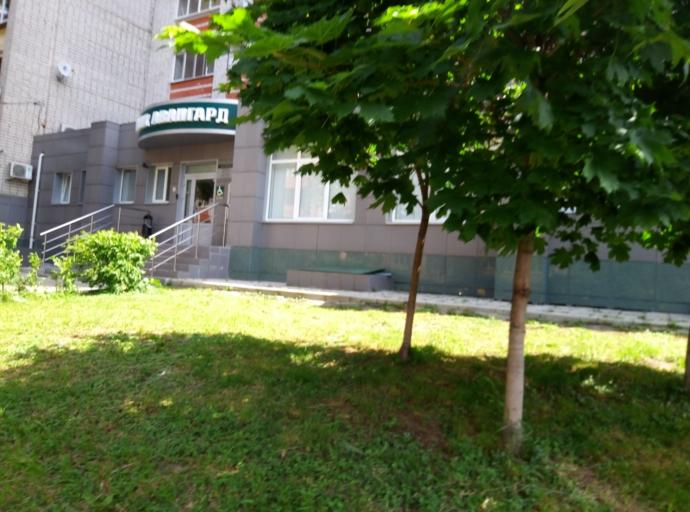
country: RU
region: Kursk
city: Kursk
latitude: 51.7393
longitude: 36.1872
